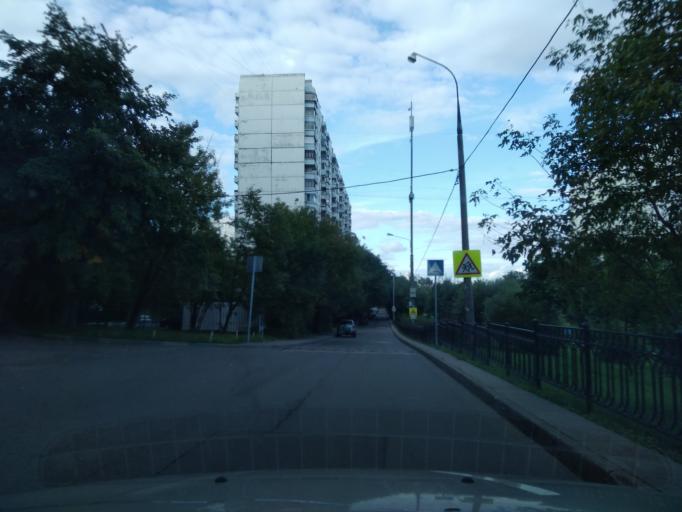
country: RU
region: Moscow
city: Strogino
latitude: 55.8147
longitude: 37.3999
